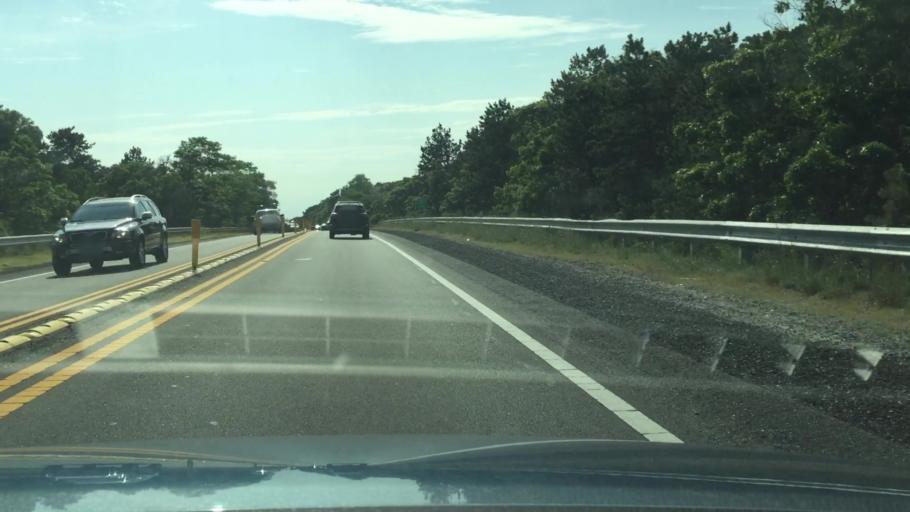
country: US
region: Massachusetts
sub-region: Barnstable County
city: Northwest Harwich
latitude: 41.7010
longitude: -70.1181
